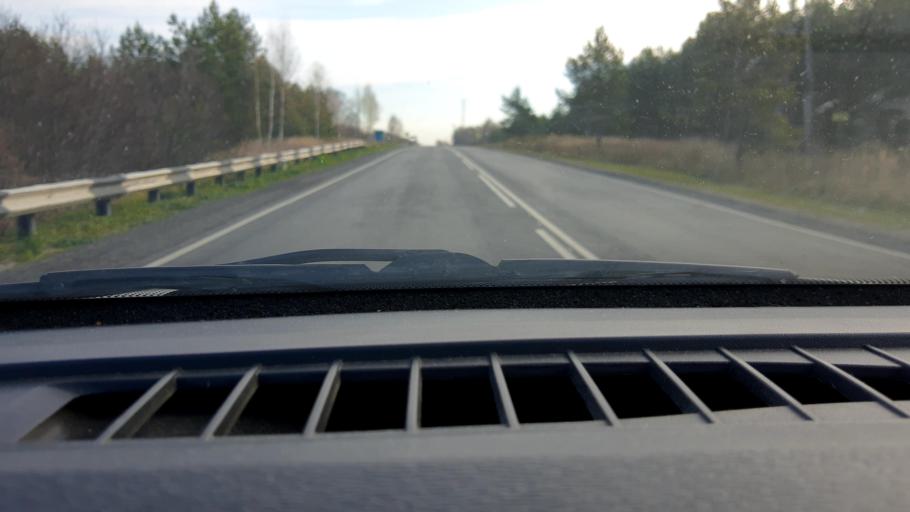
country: RU
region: Nizjnij Novgorod
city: Novaya Balakhna
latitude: 56.6050
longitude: 43.6205
